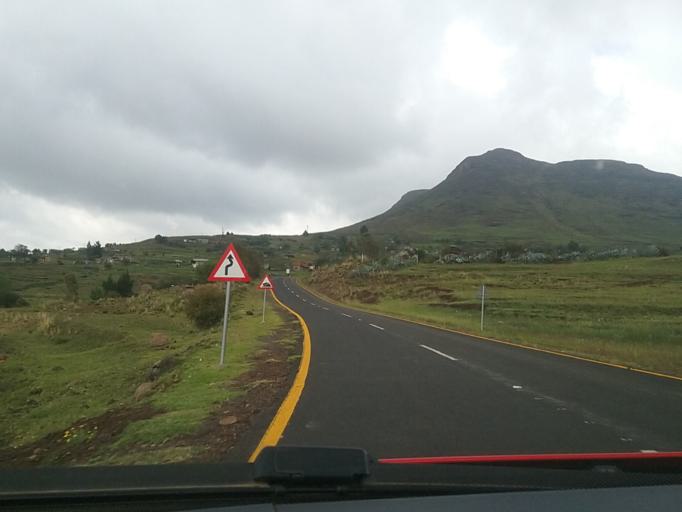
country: LS
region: Berea
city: Teyateyaneng
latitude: -29.2479
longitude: 27.8482
